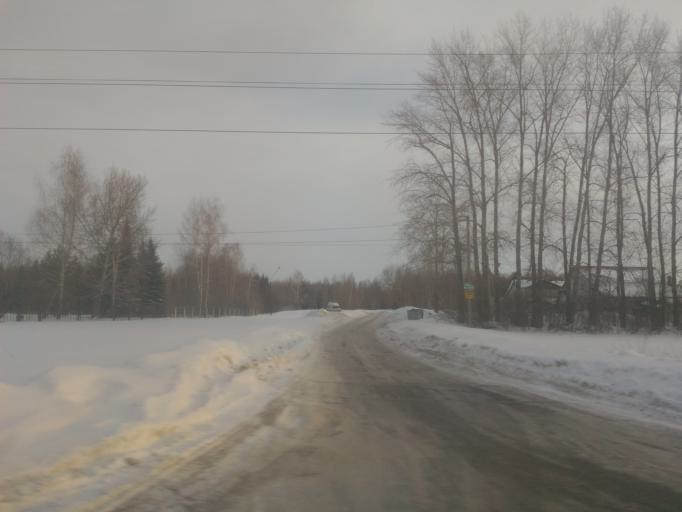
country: RU
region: Ulyanovsk
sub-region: Ulyanovskiy Rayon
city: Ulyanovsk
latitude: 54.3614
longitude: 48.3413
